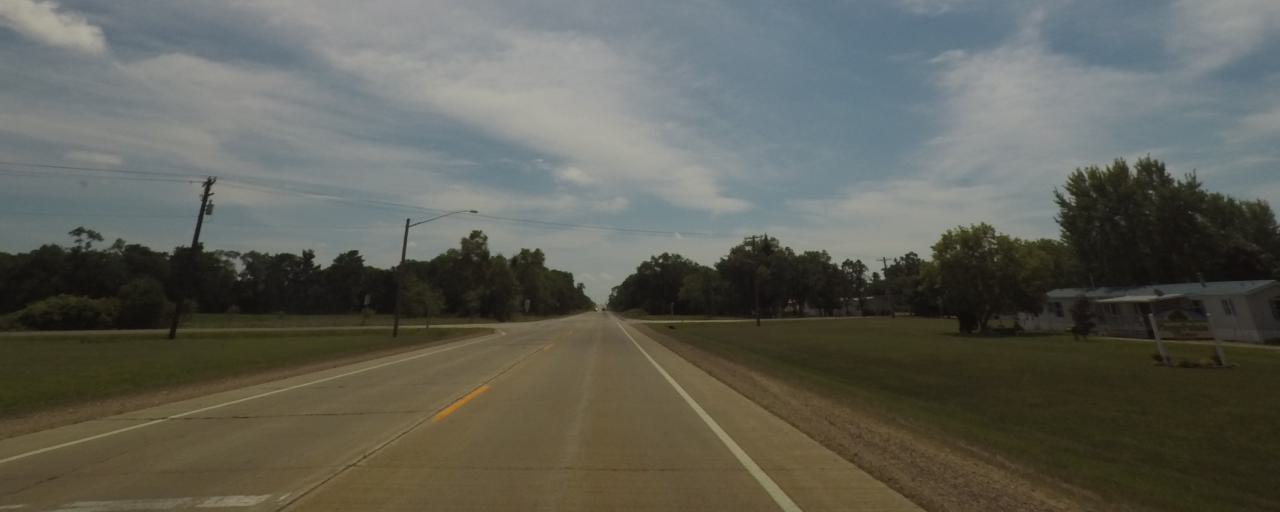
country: US
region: Wisconsin
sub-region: Portage County
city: Plover
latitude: 44.4382
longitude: -89.5295
